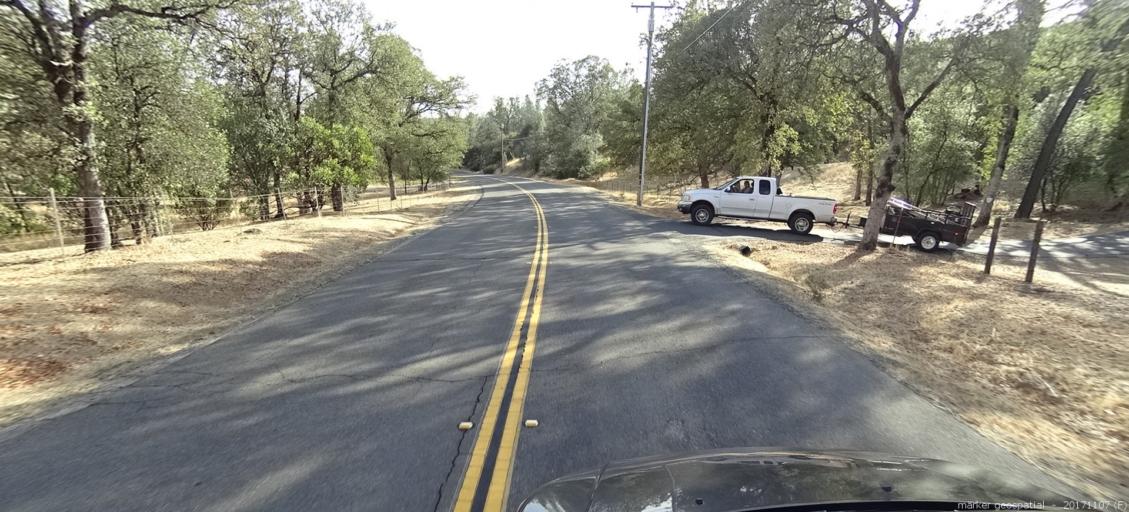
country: US
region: California
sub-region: Shasta County
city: Shasta
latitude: 40.5158
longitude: -122.4560
